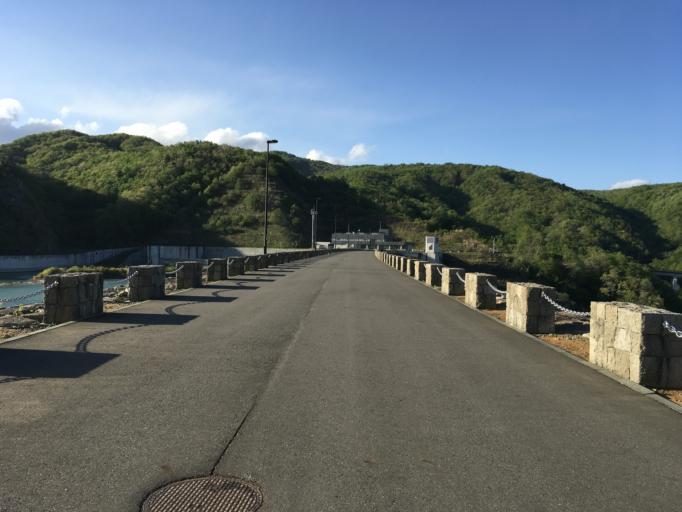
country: JP
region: Iwate
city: Mizusawa
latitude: 39.1216
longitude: 140.9198
